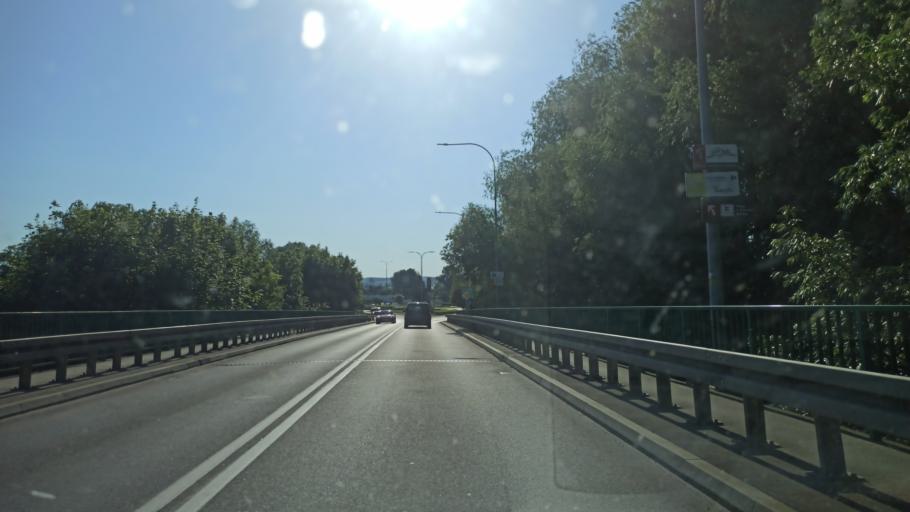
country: PL
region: Warmian-Masurian Voivodeship
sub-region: Powiat elblaski
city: Elblag
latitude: 54.1664
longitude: 19.3726
